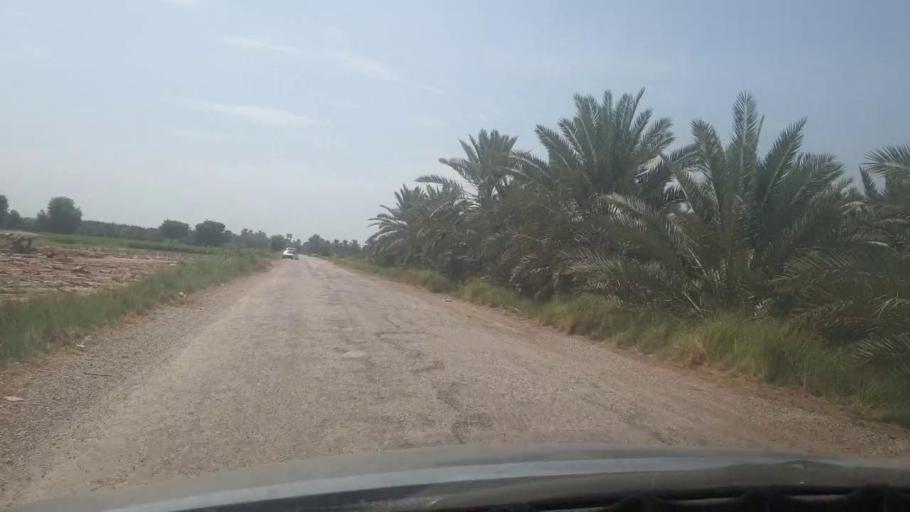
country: PK
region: Sindh
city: Bozdar
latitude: 27.2043
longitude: 68.5811
